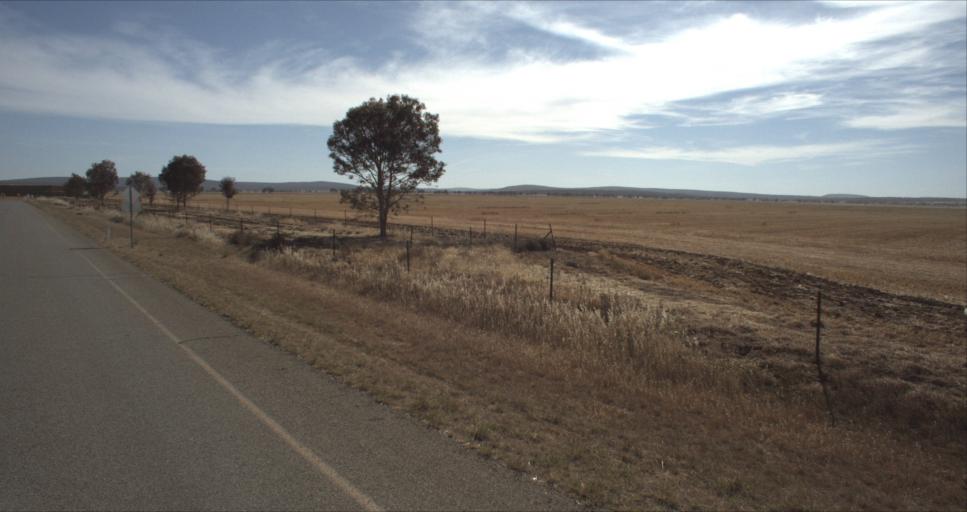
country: AU
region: New South Wales
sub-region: Leeton
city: Leeton
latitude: -34.5622
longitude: 146.4815
